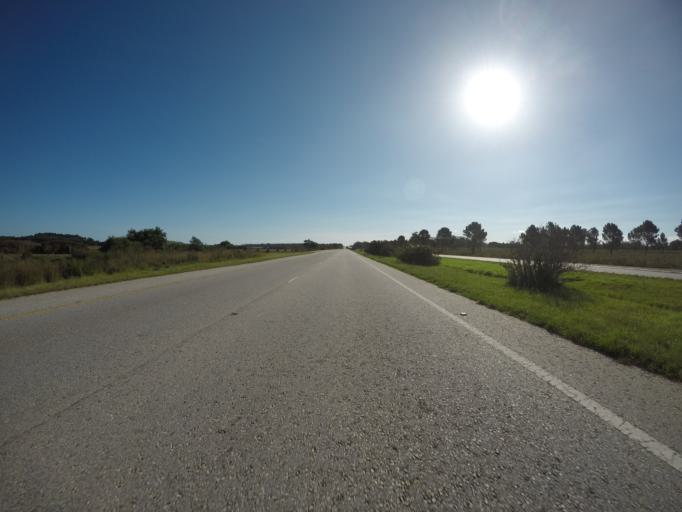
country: ZA
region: Eastern Cape
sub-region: Nelson Mandela Bay Metropolitan Municipality
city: Uitenhage
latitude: -33.9295
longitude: 25.3379
